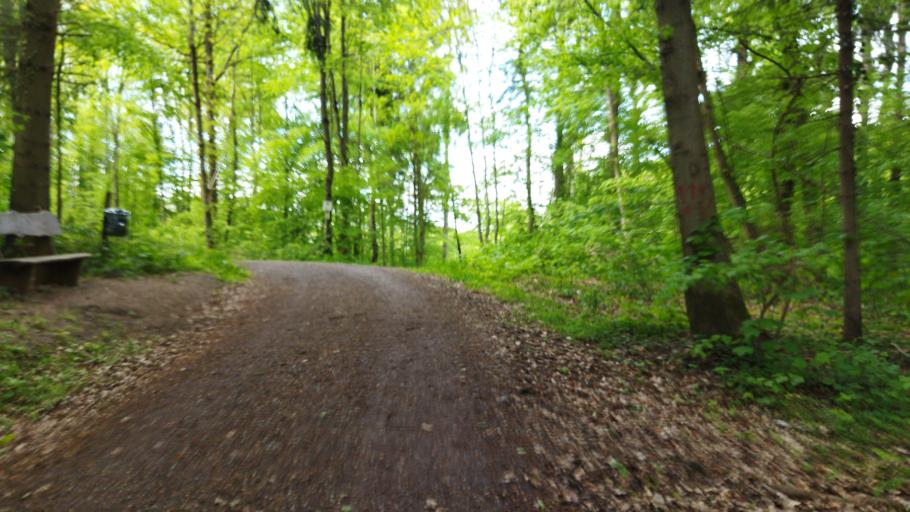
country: DE
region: Baden-Wuerttemberg
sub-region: Regierungsbezirk Stuttgart
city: Bad Rappenau
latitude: 49.2082
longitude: 9.1147
